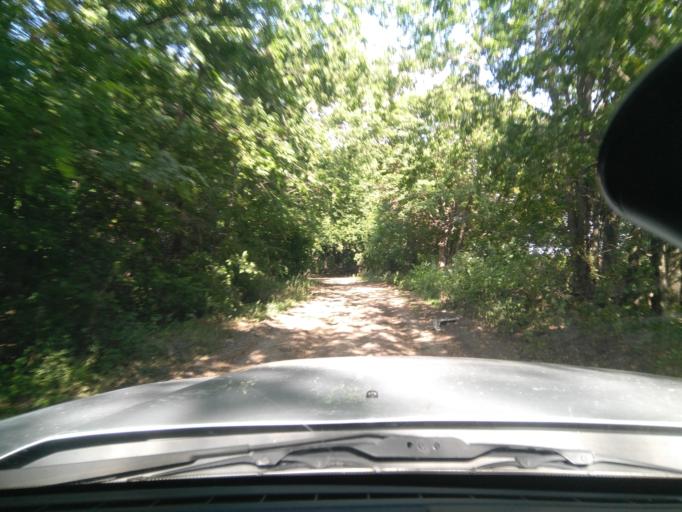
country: HU
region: Fejer
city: Bicske
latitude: 47.4414
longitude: 18.6485
